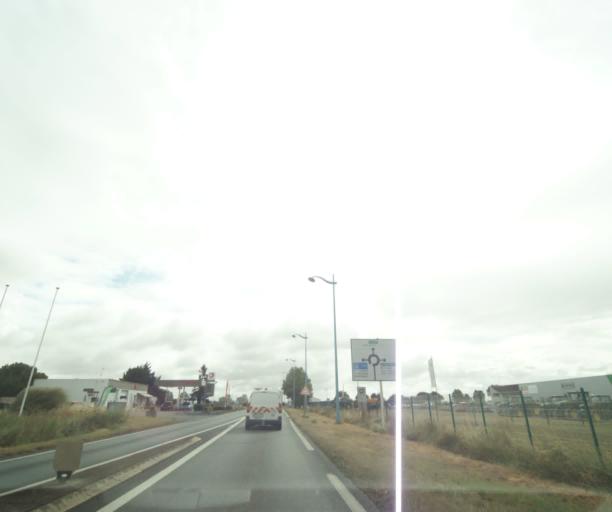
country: FR
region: Pays de la Loire
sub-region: Departement de la Vendee
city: Sainte-Gemme-la-Plaine
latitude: 46.4668
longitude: -1.1116
